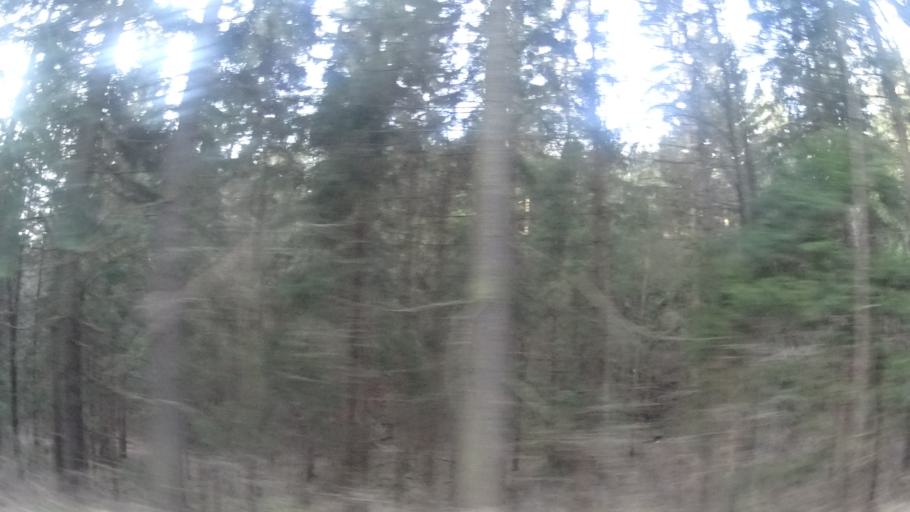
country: DE
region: Thuringia
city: Rottenbach
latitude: 50.7292
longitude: 11.1987
